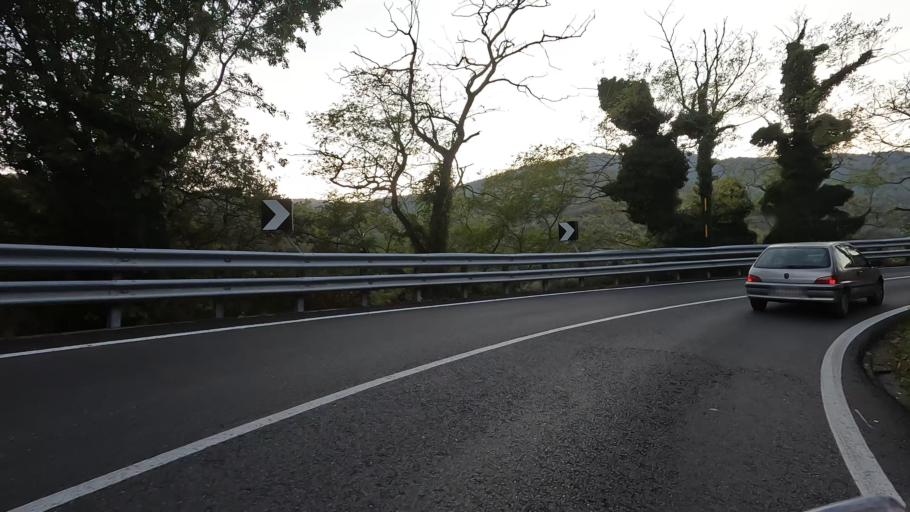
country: IT
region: Liguria
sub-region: Provincia di Savona
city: Osteria dei Cacciatori-Stella
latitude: 44.4195
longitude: 8.4786
